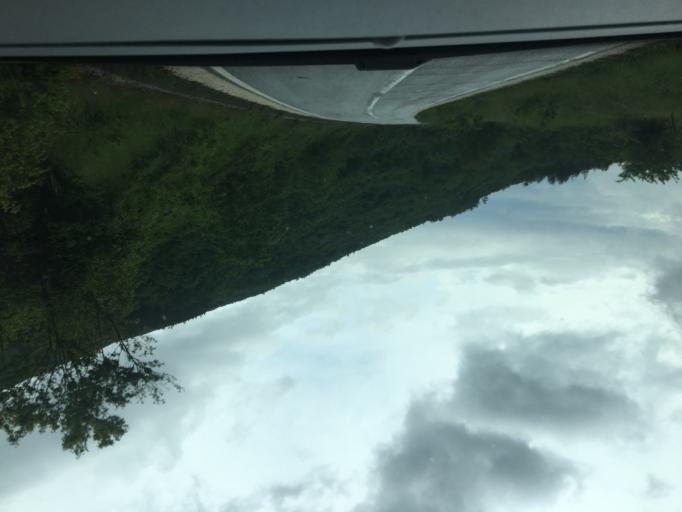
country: MK
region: Debarca
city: Meseista
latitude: 41.2718
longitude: 20.7815
